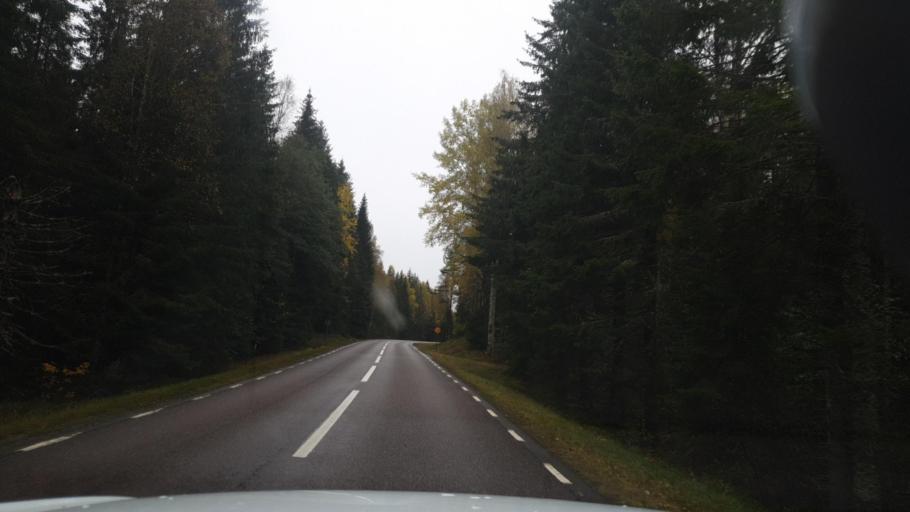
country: SE
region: Vaermland
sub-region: Eda Kommun
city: Amotfors
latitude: 59.6444
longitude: 12.3558
